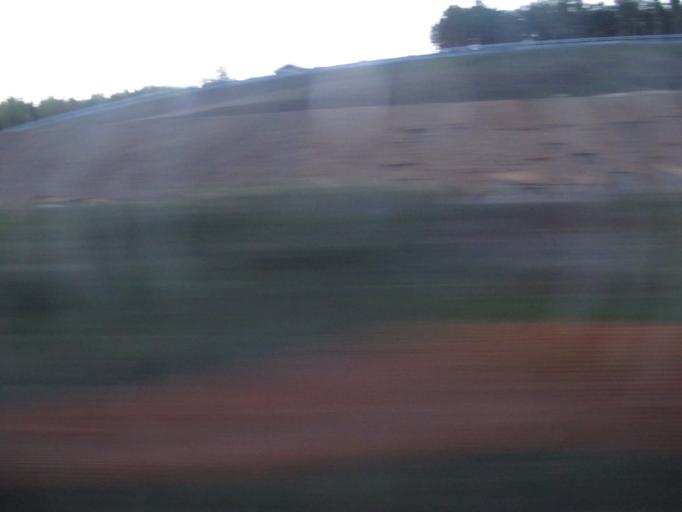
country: NO
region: Oppland
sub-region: Sor-Fron
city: Hundorp
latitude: 61.5629
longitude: 9.9237
